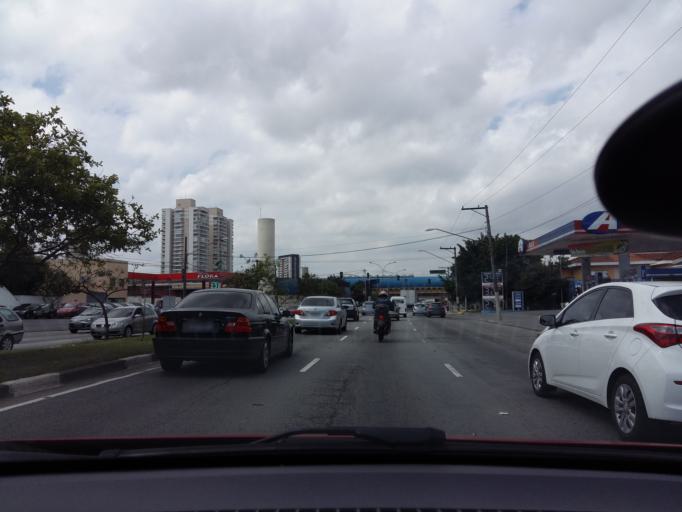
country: BR
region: Sao Paulo
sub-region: Sao Caetano Do Sul
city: Sao Caetano do Sul
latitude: -23.6061
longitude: -46.6051
